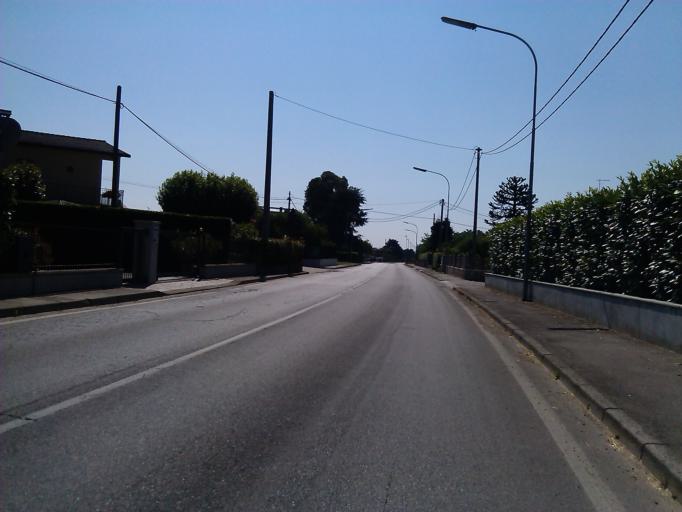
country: IT
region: Veneto
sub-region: Provincia di Vicenza
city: Cassola
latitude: 45.7498
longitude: 11.7973
